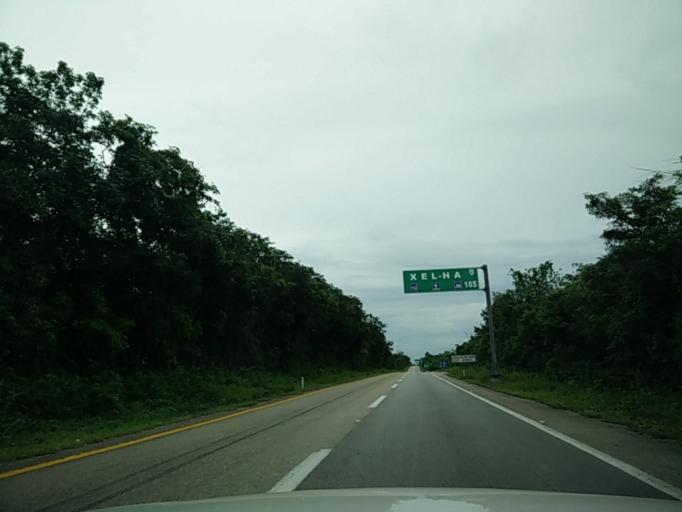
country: MX
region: Quintana Roo
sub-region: Lazaro Cardenas
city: Nuevo Xcan
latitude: 20.8769
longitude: -87.6331
